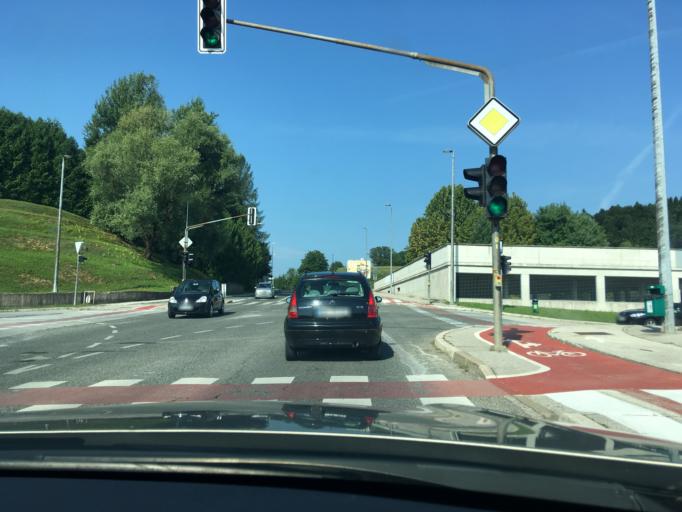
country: SI
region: Novo Mesto
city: Novo Mesto
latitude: 45.8023
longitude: 15.1596
